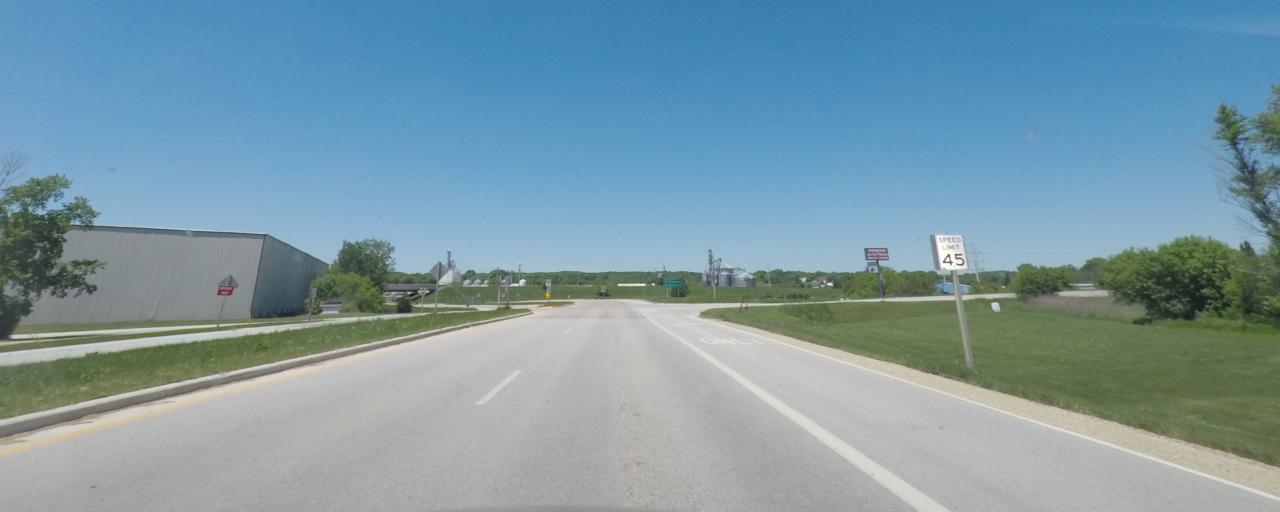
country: US
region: Wisconsin
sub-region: Washington County
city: West Bend
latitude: 43.4546
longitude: -88.2004
